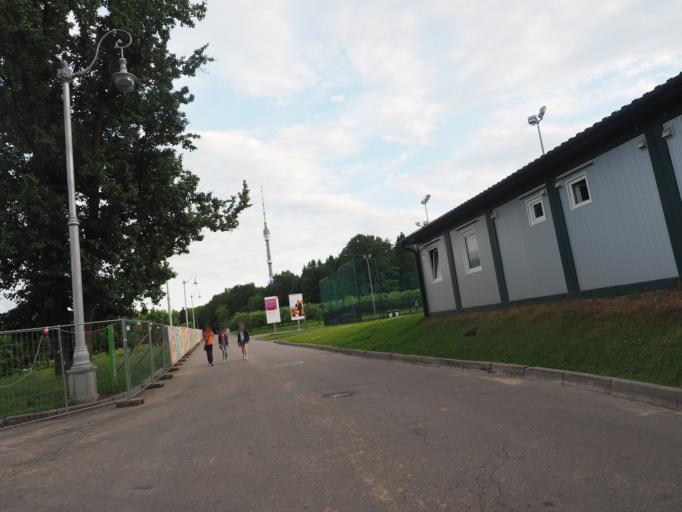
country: RU
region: Moscow
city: Ostankinskiy
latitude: 55.8350
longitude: 37.6156
